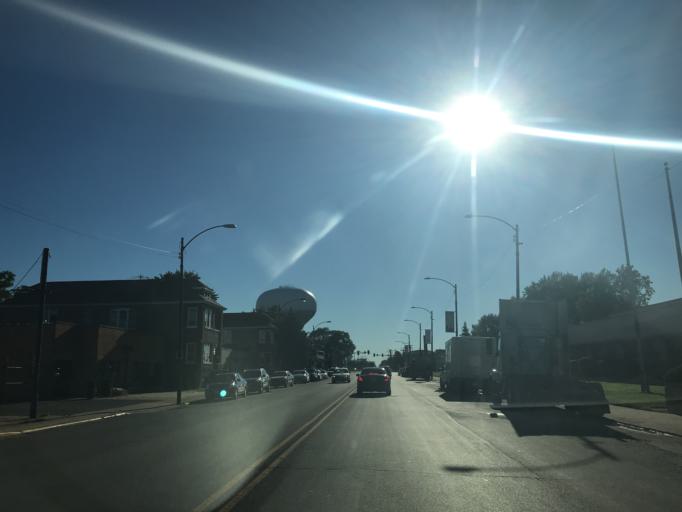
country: US
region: Illinois
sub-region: Cook County
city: Cicero
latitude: 41.8658
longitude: -87.7518
